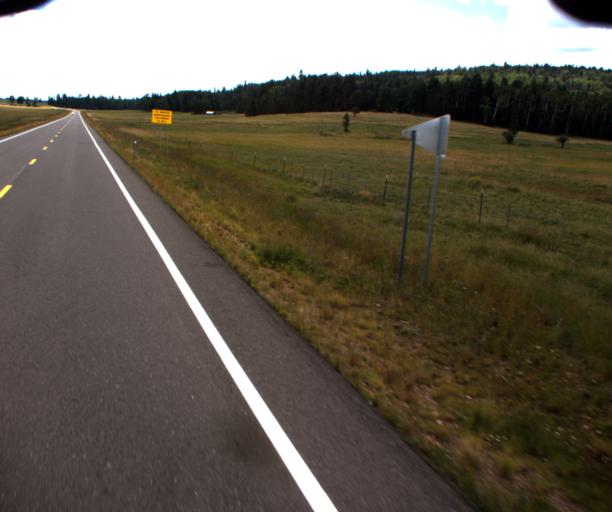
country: US
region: Arizona
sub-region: Apache County
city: Eagar
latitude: 33.9993
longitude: -109.5260
